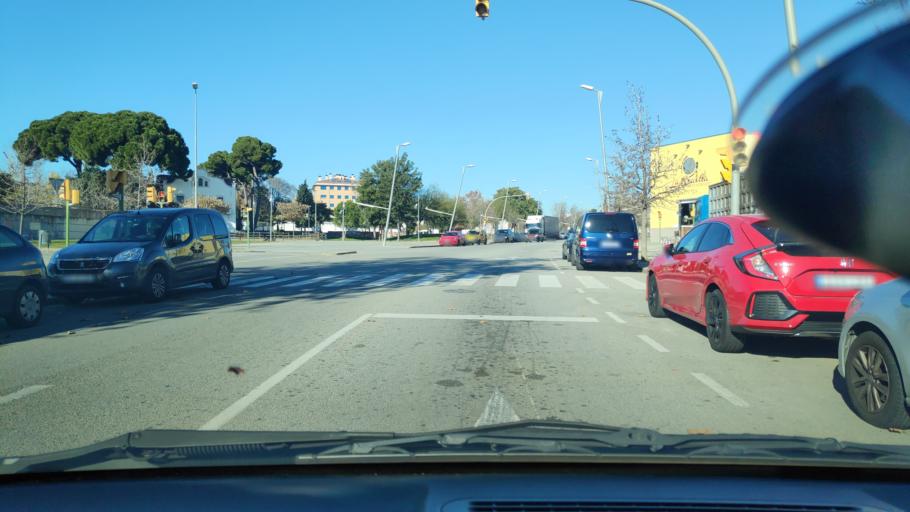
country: ES
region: Catalonia
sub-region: Provincia de Barcelona
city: Sant Quirze del Valles
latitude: 41.5421
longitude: 2.0917
